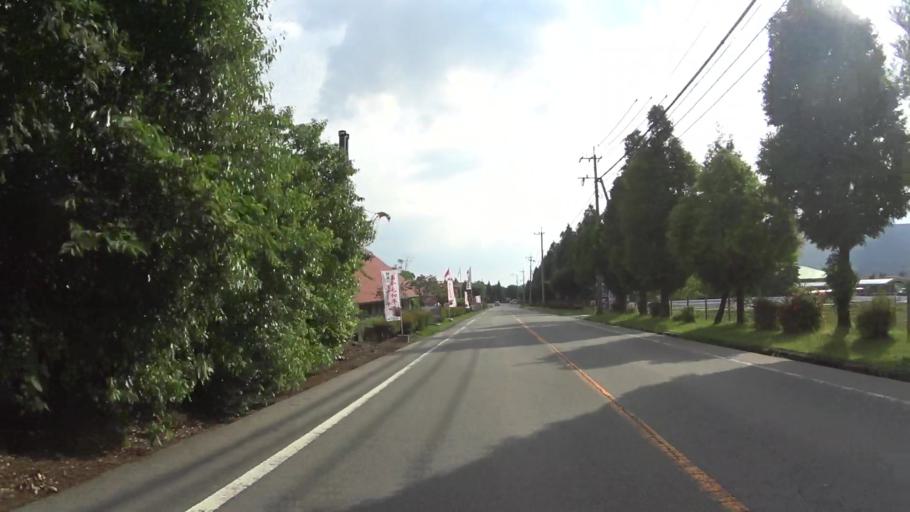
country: JP
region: Kumamoto
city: Aso
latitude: 32.8989
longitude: 131.0099
